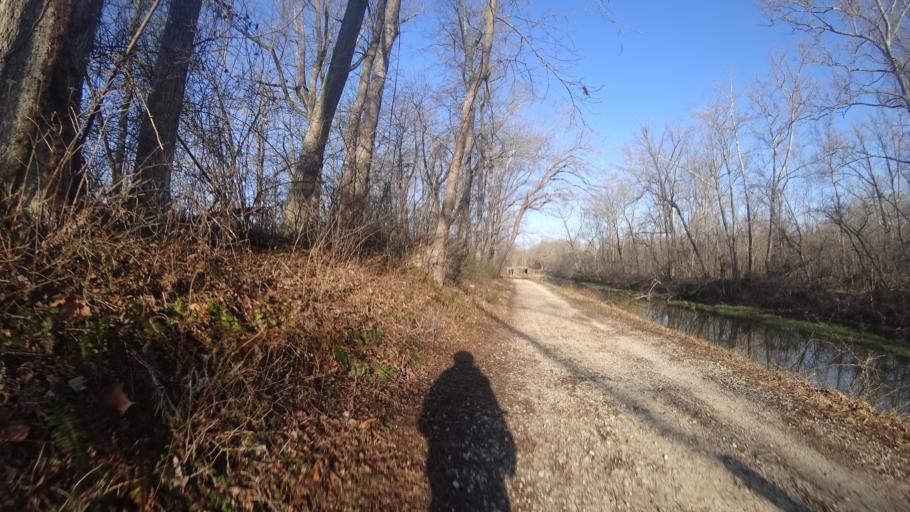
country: US
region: Virginia
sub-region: Loudoun County
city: Lowes Island
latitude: 39.0662
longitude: -77.3261
